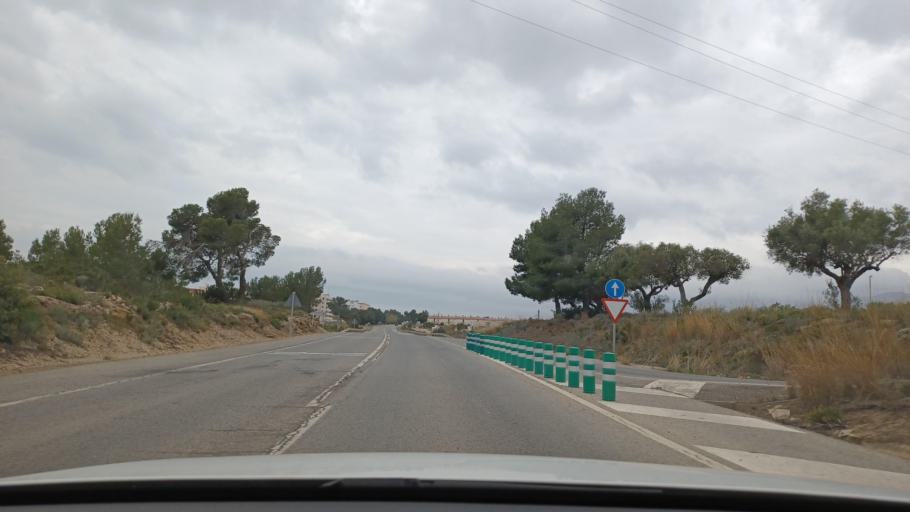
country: ES
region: Catalonia
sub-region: Provincia de Tarragona
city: Vilanova d'Escornalbou
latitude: 41.0238
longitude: 0.9558
